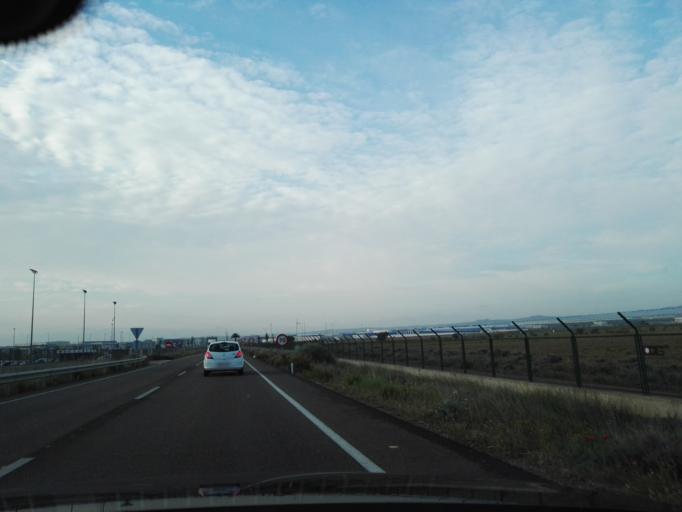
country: ES
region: Aragon
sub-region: Provincia de Zaragoza
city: Utebo
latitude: 41.6566
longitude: -1.0016
